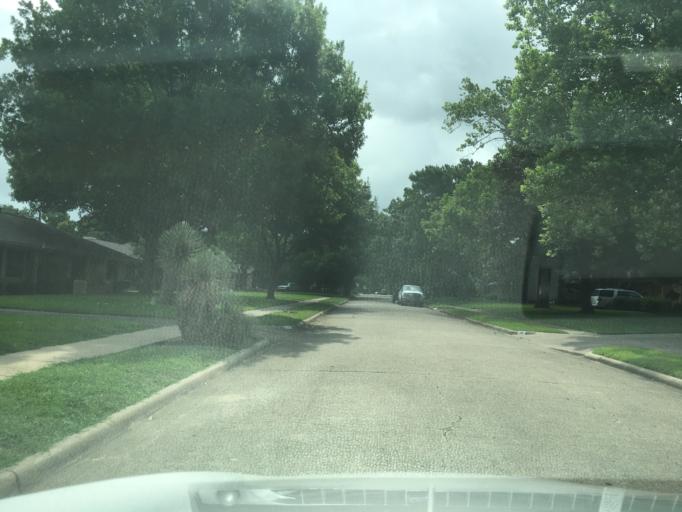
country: US
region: Texas
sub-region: Dallas County
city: Richardson
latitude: 32.9418
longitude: -96.7199
